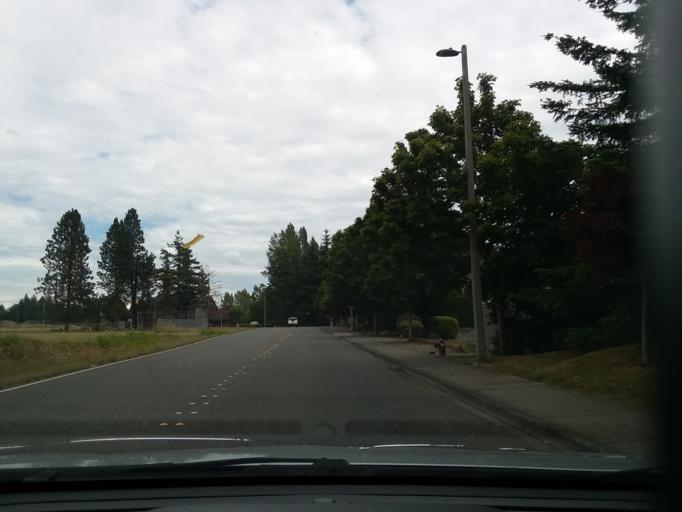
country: US
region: Washington
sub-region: Whatcom County
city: Bellingham
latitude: 48.7878
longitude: -122.4803
